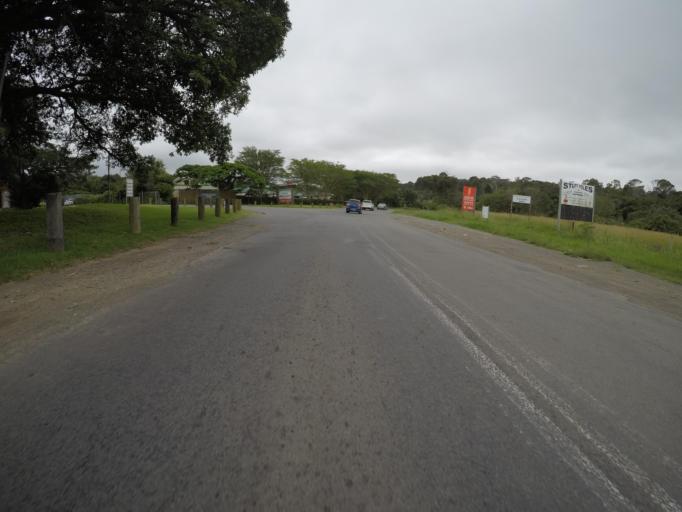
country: ZA
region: Eastern Cape
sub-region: Buffalo City Metropolitan Municipality
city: East London
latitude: -32.9392
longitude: 27.9395
